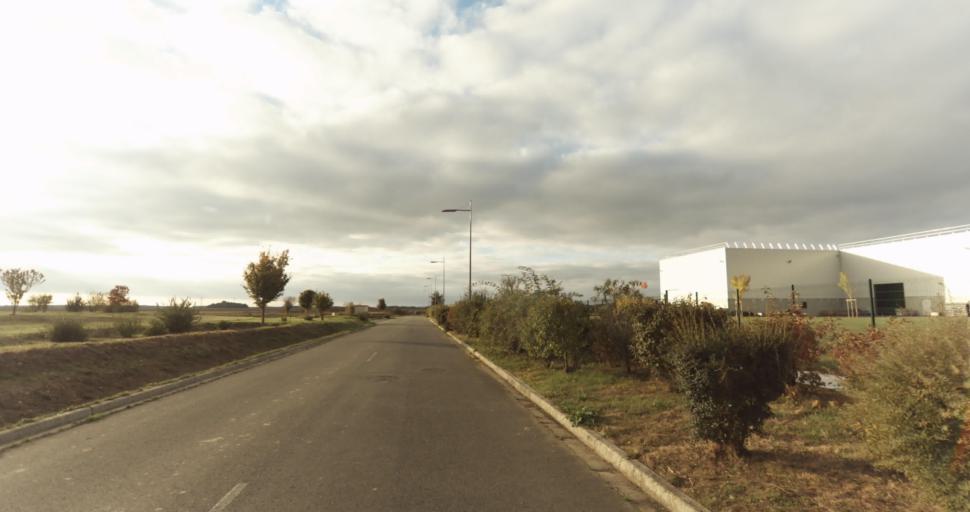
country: FR
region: Centre
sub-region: Departement d'Eure-et-Loir
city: Vernouillet
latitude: 48.7089
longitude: 1.3763
